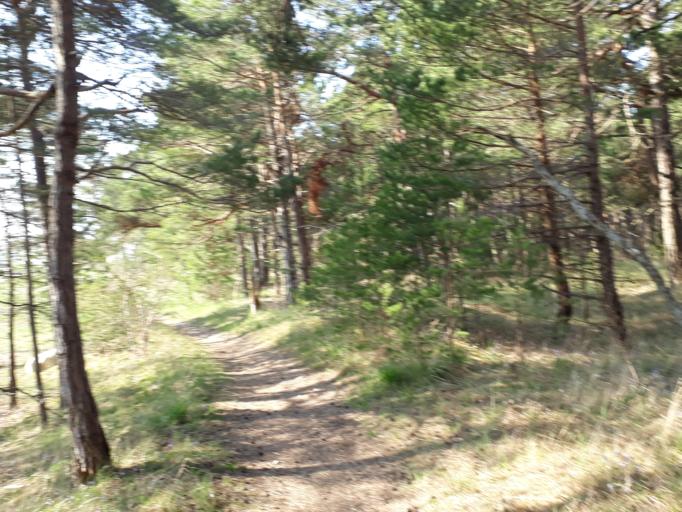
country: SE
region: Gotland
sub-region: Gotland
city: Visby
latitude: 57.6719
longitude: 18.3358
